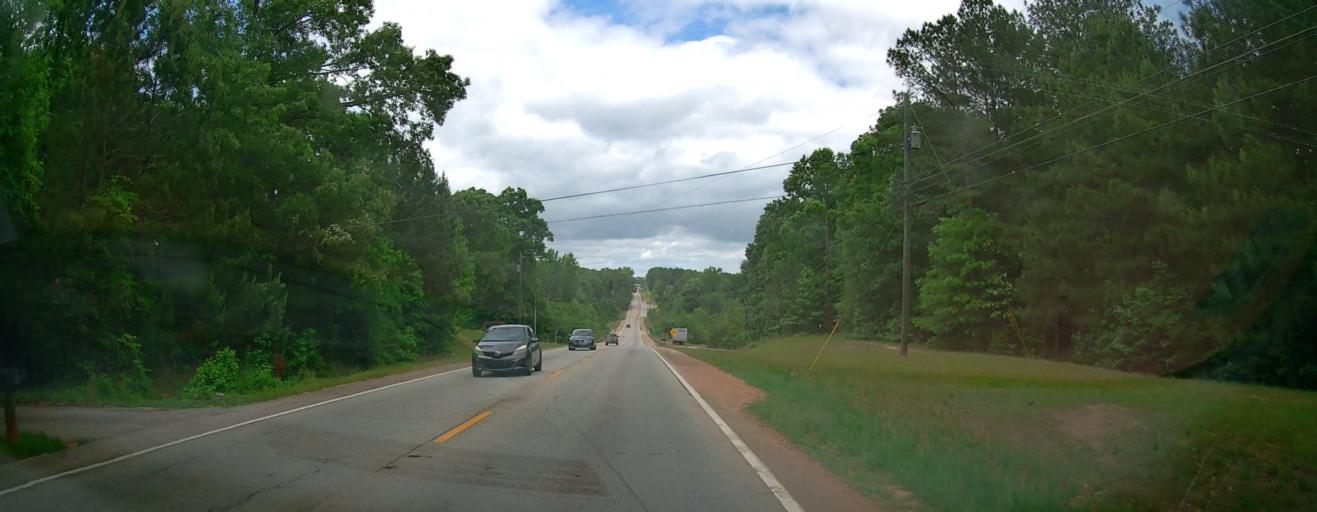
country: US
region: Georgia
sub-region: Henry County
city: Stockbridge
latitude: 33.5494
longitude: -84.1814
